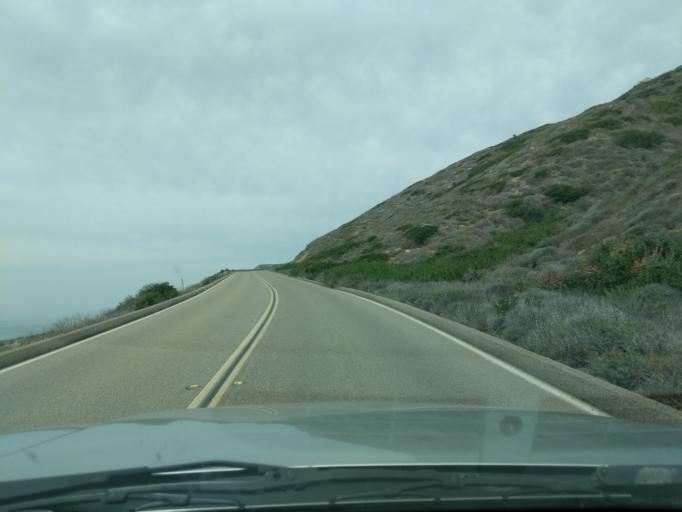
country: US
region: California
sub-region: San Diego County
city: Coronado
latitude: 32.6688
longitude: -117.2430
